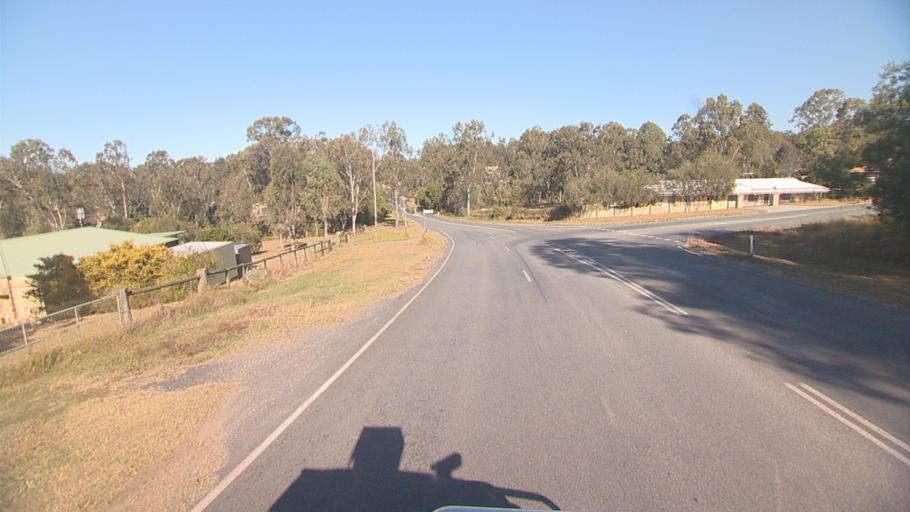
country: AU
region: Queensland
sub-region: Logan
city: Cedar Vale
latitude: -27.8603
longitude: 153.0370
